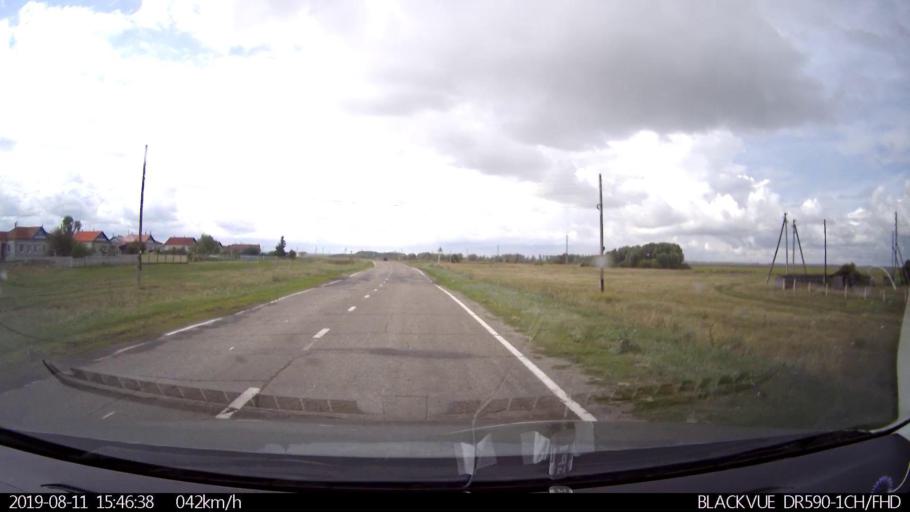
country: RU
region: Ulyanovsk
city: Ignatovka
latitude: 53.8832
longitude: 47.6553
